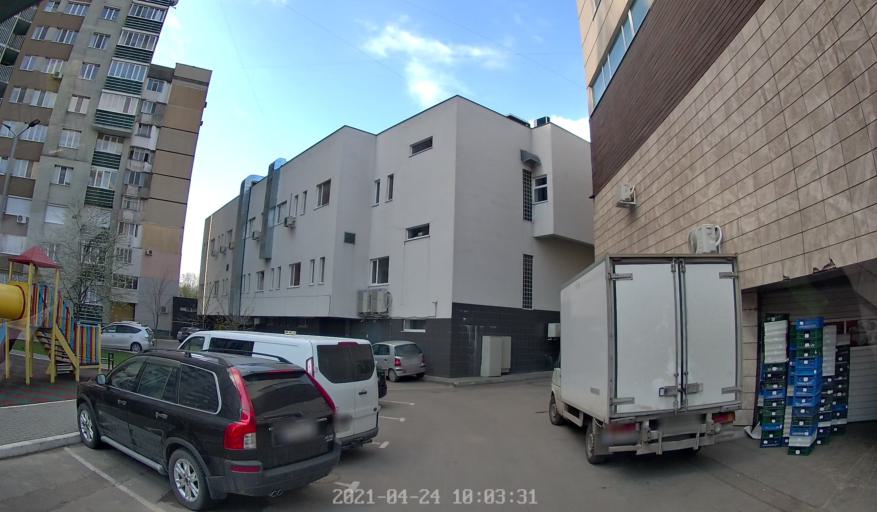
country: NG
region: Niger
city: Lemu
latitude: 9.4112
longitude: 5.7785
